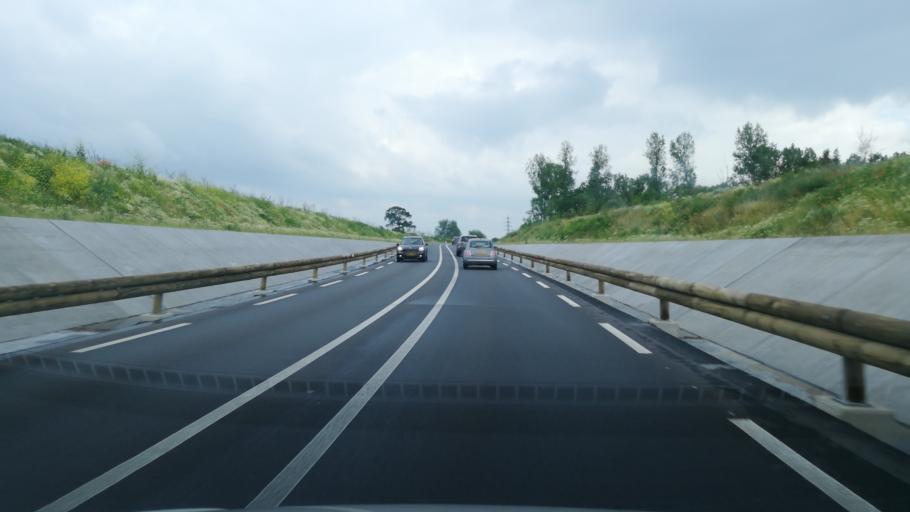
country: NL
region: Gelderland
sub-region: Gemeente Voorst
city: Voorst
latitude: 52.1668
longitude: 6.1335
